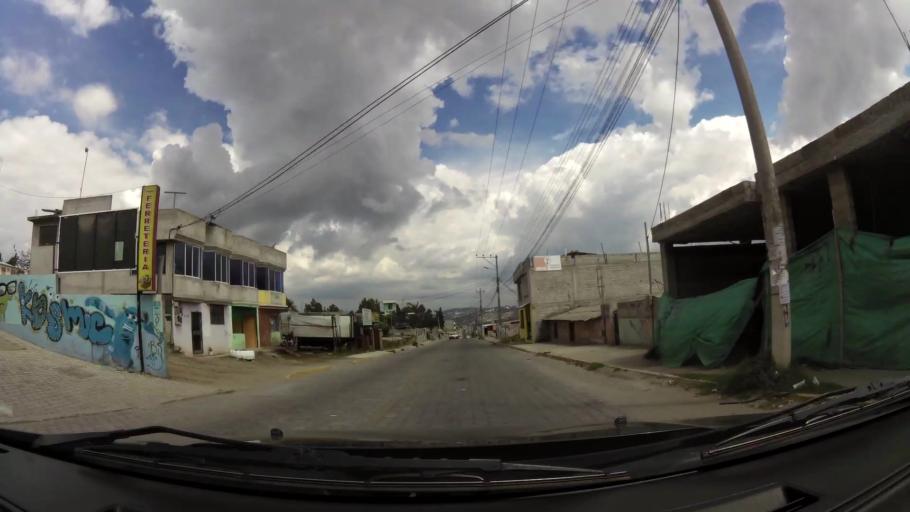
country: EC
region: Pichincha
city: Quito
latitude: -0.0769
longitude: -78.4354
